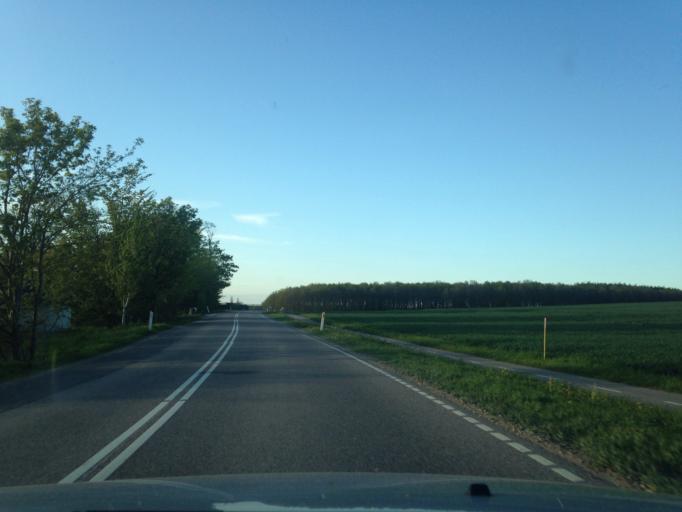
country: DK
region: Capital Region
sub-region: Hoje-Taastrup Kommune
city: Flong
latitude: 55.6341
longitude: 12.1933
